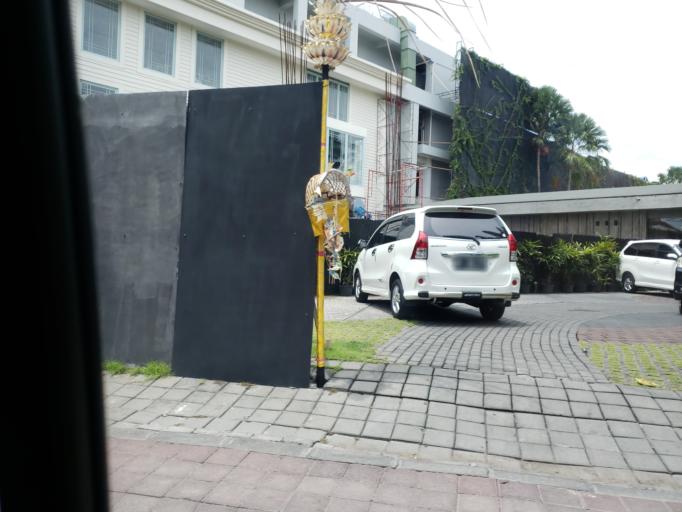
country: ID
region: Bali
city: Kuta
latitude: -8.6767
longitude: 115.1552
